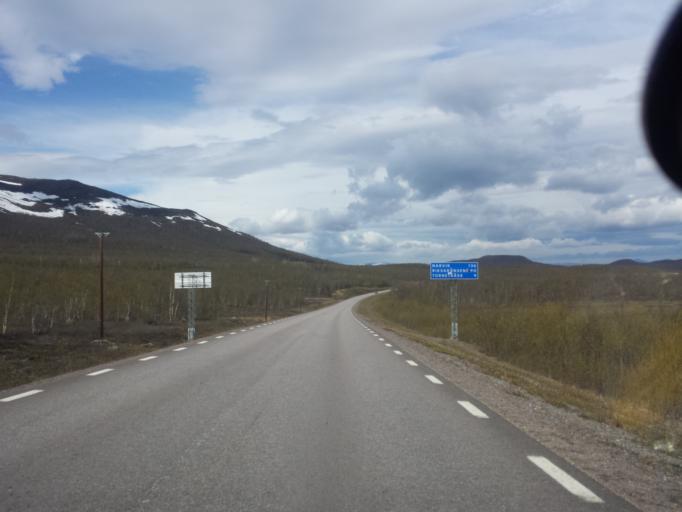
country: SE
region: Norrbotten
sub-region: Kiruna Kommun
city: Kiruna
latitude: 68.1598
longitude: 19.7782
